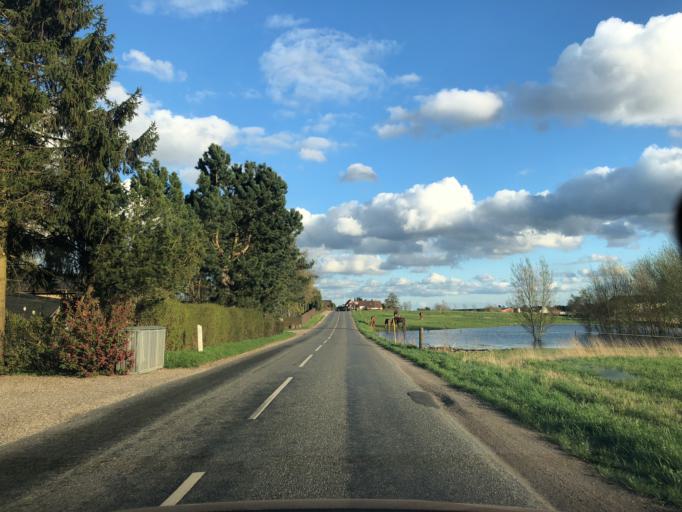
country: DK
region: Zealand
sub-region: Ringsted Kommune
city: Ringsted
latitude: 55.4969
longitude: 11.8618
